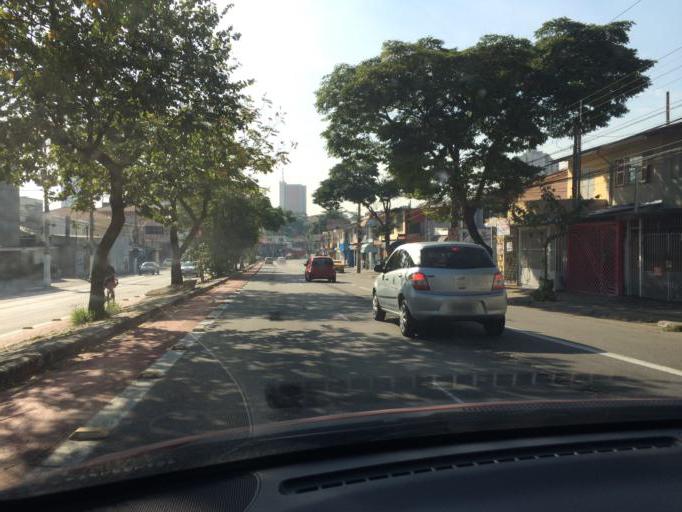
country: BR
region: Sao Paulo
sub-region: Osasco
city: Osasco
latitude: -23.5554
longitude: -46.7537
